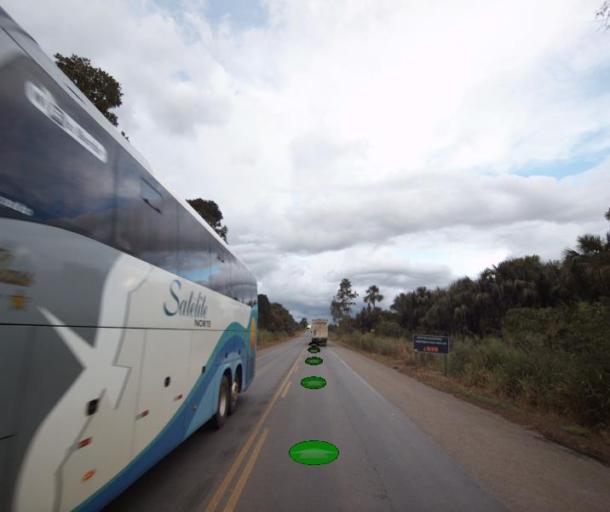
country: BR
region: Goias
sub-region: Itapaci
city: Itapaci
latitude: -14.8074
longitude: -49.2893
